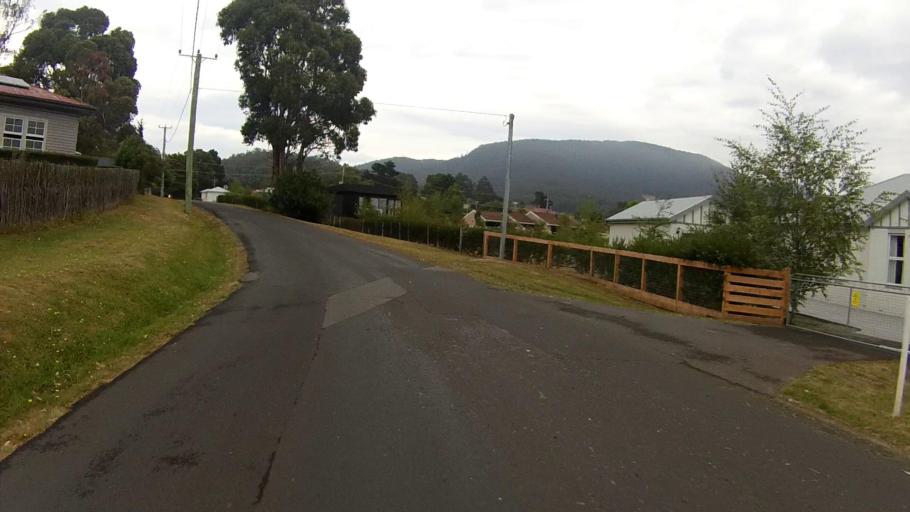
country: AU
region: Tasmania
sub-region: Kingborough
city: Kettering
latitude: -43.1595
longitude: 147.2372
